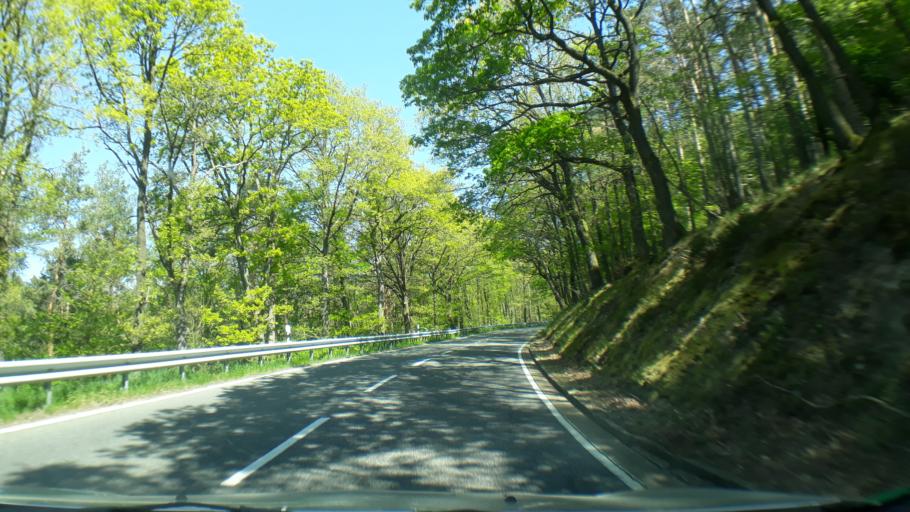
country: DE
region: North Rhine-Westphalia
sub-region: Regierungsbezirk Koln
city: Nideggen
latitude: 50.6841
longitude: 6.4298
